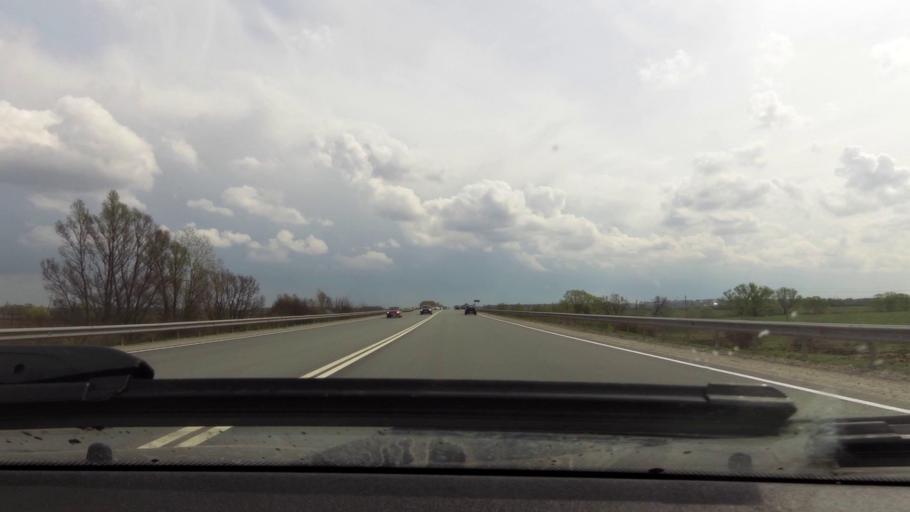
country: RU
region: Rjazan
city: Bagramovo
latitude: 54.7452
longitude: 39.4363
